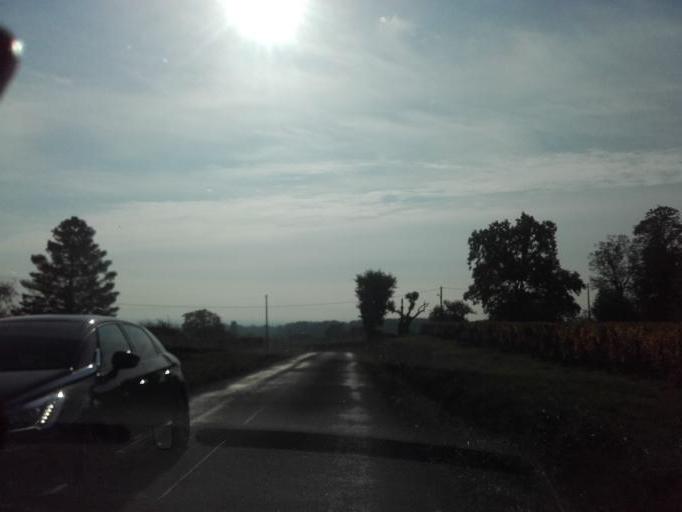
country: FR
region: Bourgogne
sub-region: Departement de Saone-et-Loire
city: Creches-sur-Saone
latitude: 46.2507
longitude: 4.7636
